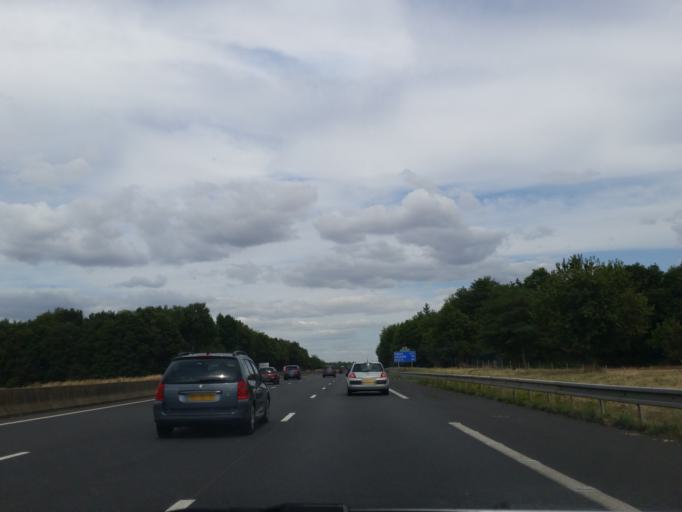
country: FR
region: Centre
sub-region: Departement d'Indre-et-Loire
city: Monnaie
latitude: 47.4802
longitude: 0.7879
